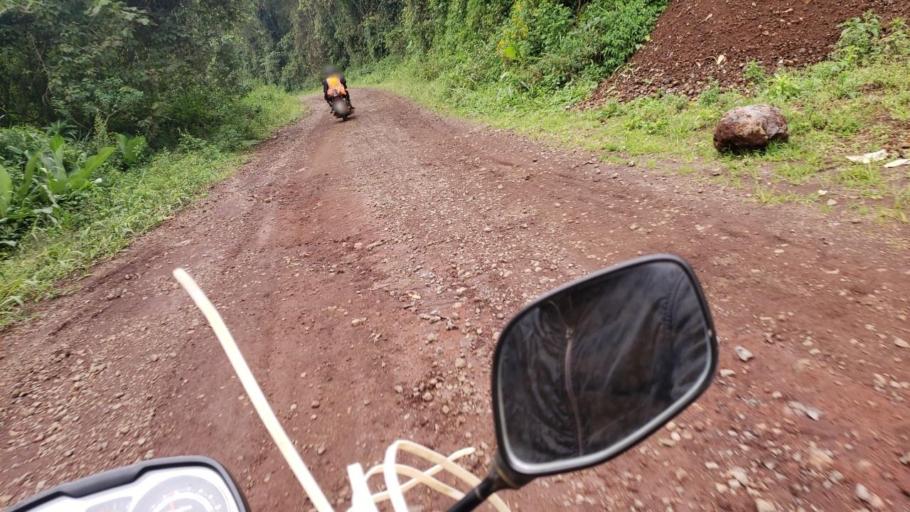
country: CD
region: South Kivu
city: Kabare
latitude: -2.3140
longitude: 28.7496
